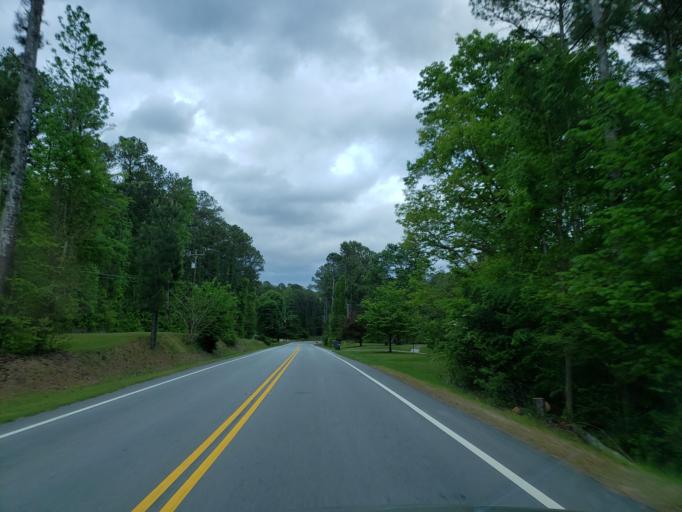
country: US
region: Georgia
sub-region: Paulding County
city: Dallas
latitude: 33.8733
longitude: -84.8620
